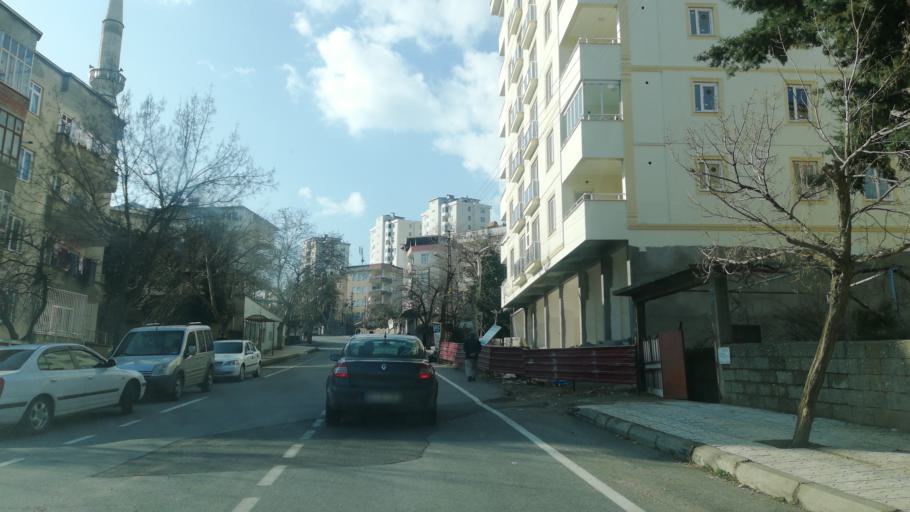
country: TR
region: Kahramanmaras
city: Kahramanmaras
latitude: 37.5916
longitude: 36.9046
